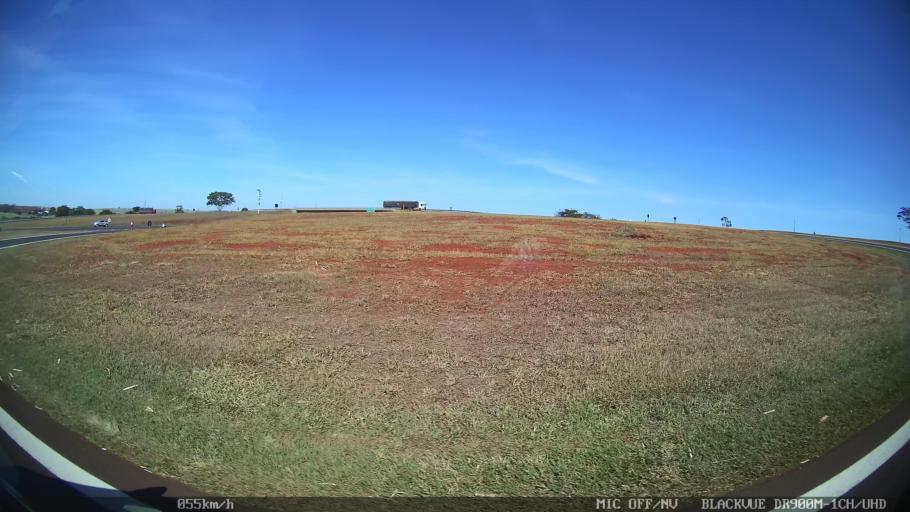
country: BR
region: Sao Paulo
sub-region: Sao Joaquim Da Barra
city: Sao Joaquim da Barra
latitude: -20.5230
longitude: -47.8416
